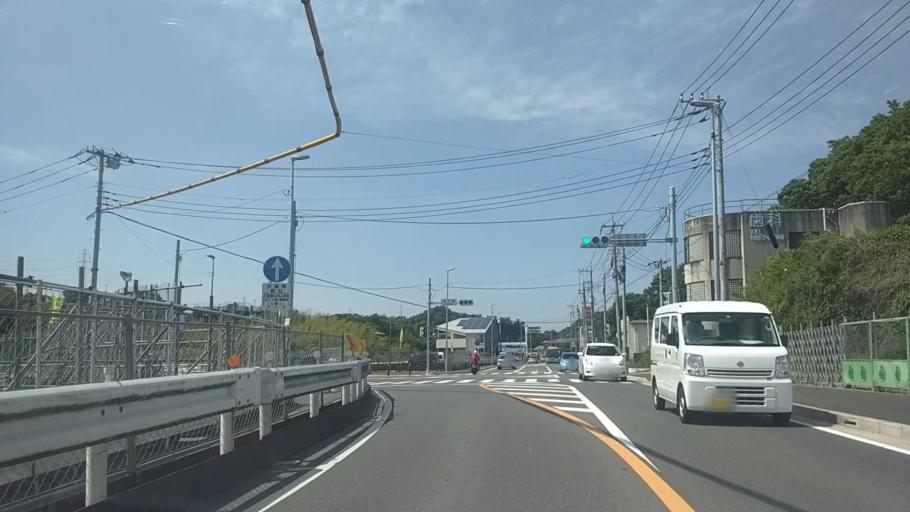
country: JP
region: Kanagawa
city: Kamakura
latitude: 35.3516
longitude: 139.5802
